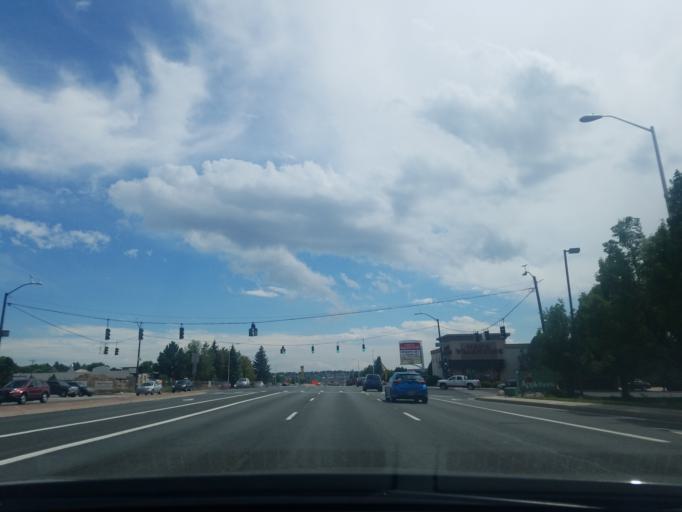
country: US
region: Colorado
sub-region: El Paso County
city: Air Force Academy
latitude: 38.9404
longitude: -104.7993
